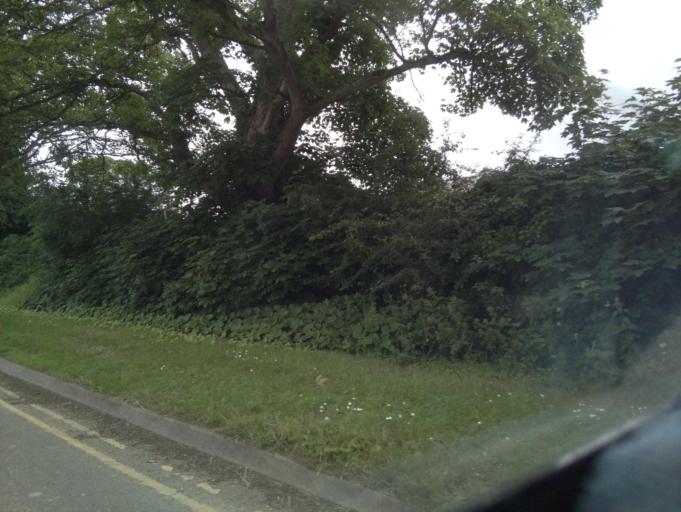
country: GB
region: England
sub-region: District of Rutland
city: Oakham
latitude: 52.6638
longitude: -0.7235
